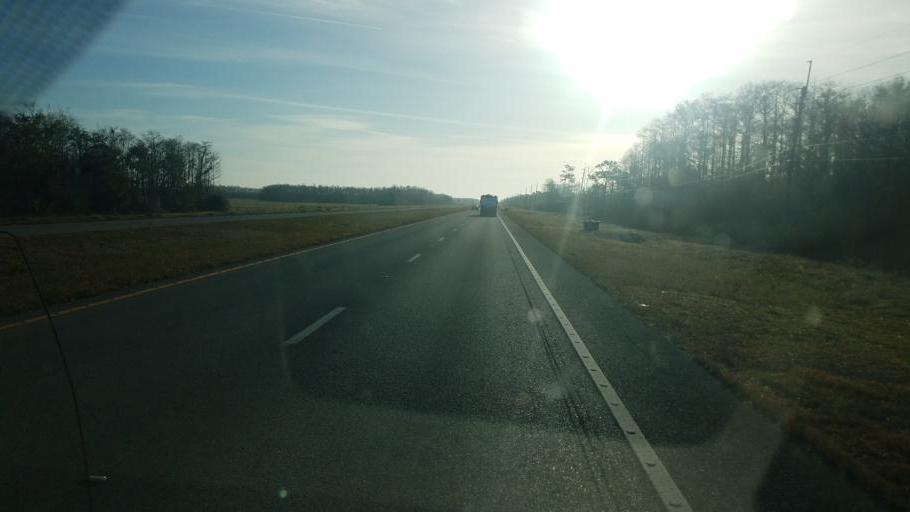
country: US
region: Florida
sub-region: Osceola County
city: Saint Cloud
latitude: 28.1435
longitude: -81.0633
